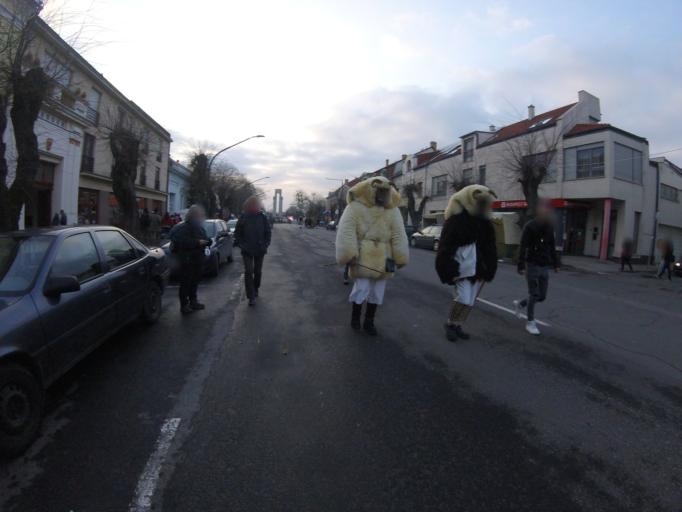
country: HU
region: Baranya
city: Mohacs
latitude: 45.9904
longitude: 18.6871
